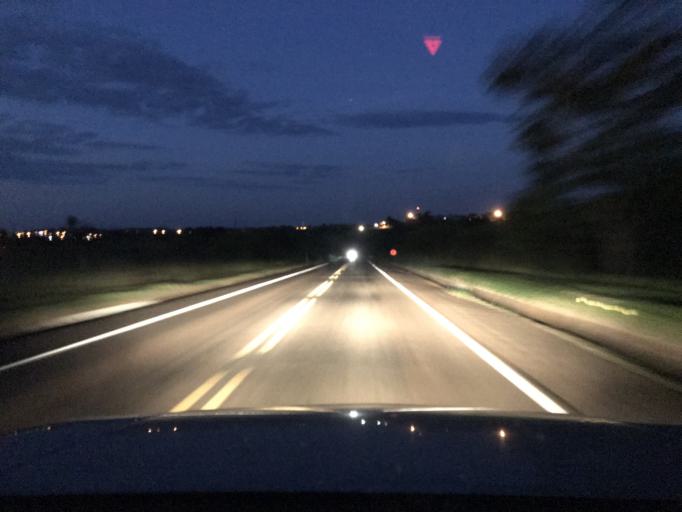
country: PY
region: Canindeyu
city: Salto del Guaira
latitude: -24.1055
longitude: -54.2372
